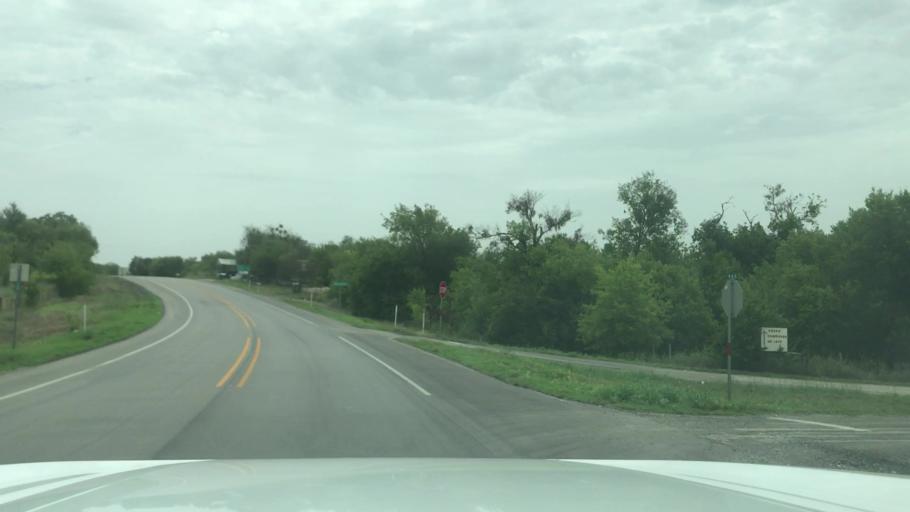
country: US
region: Texas
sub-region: Erath County
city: Dublin
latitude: 32.0597
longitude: -98.2104
